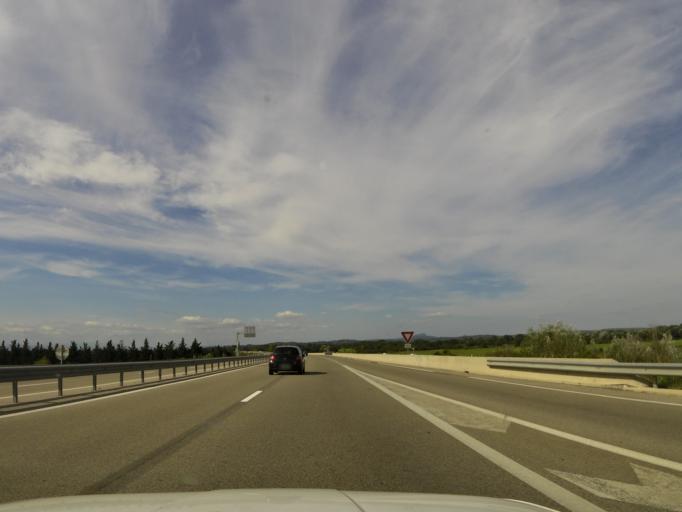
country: FR
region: Languedoc-Roussillon
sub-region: Departement du Gard
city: La Calmette
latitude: 43.9345
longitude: 4.2548
